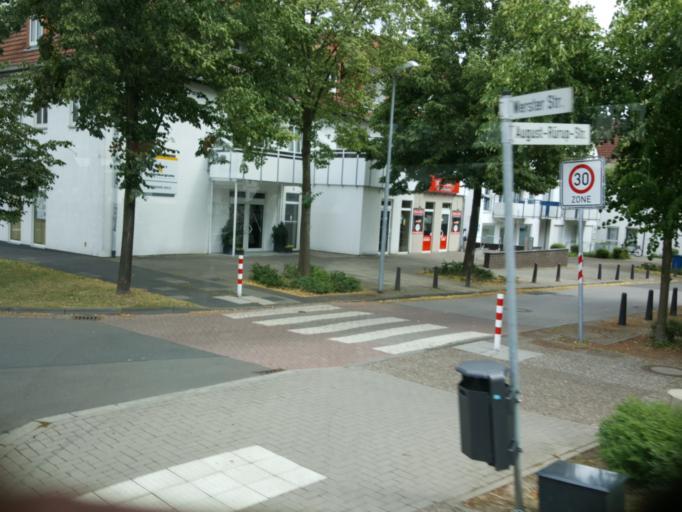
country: DE
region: North Rhine-Westphalia
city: Bad Oeynhausen
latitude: 52.2157
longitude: 8.7800
